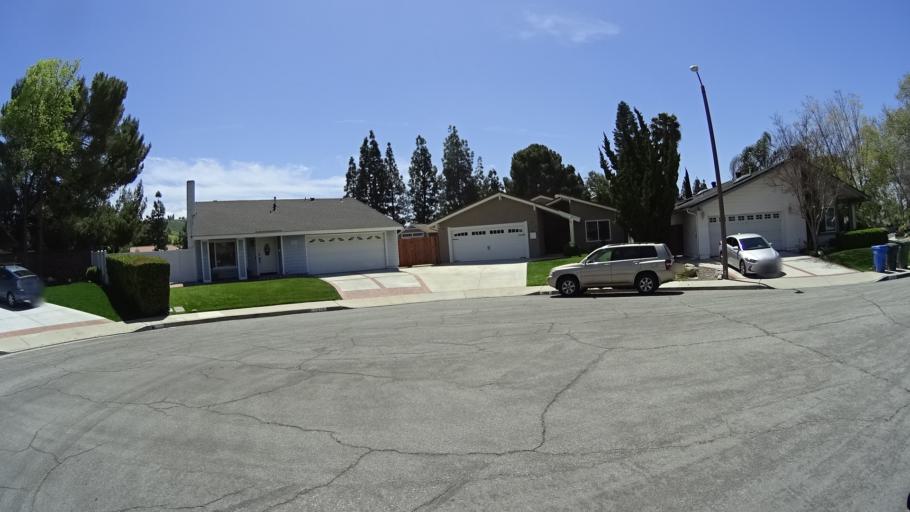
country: US
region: California
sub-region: Ventura County
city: Thousand Oaks
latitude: 34.2121
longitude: -118.8408
